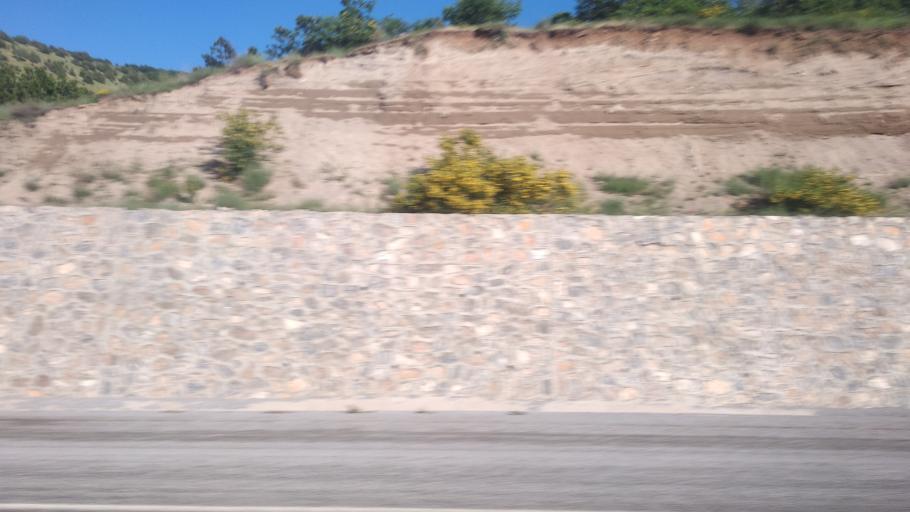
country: TR
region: Bitlis
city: Resadiye
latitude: 38.4746
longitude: 42.5275
